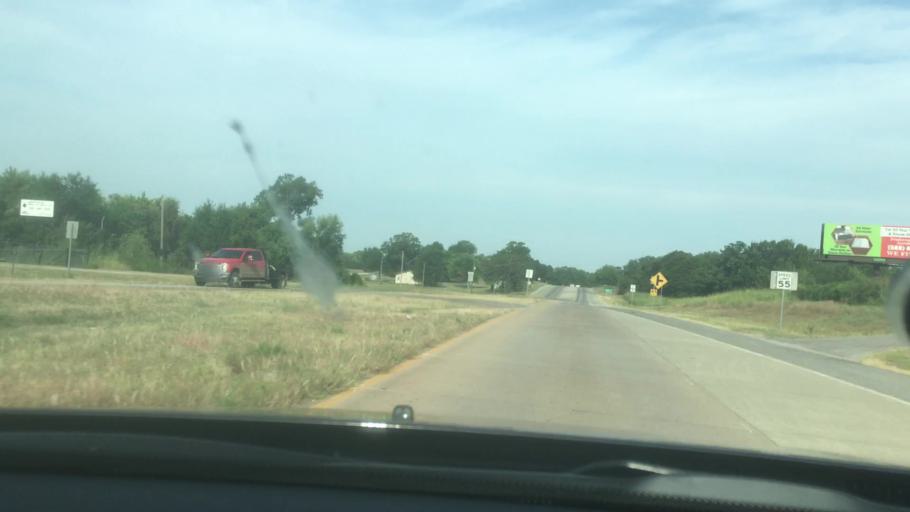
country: US
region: Oklahoma
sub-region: Pontotoc County
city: Ada
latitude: 34.7857
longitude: -96.7278
